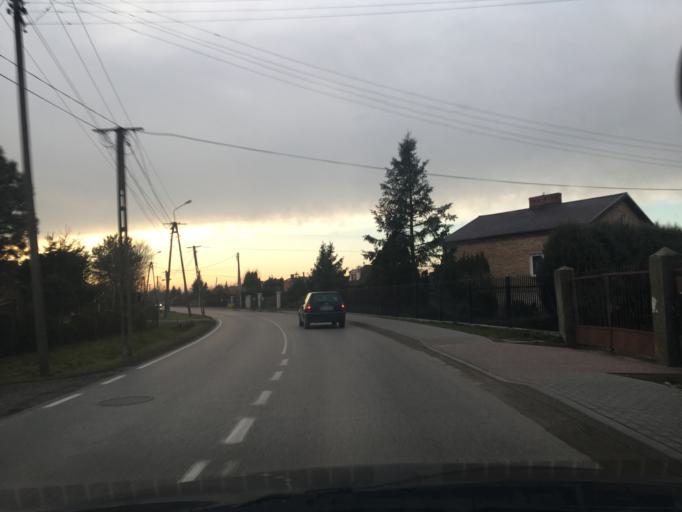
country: PL
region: Masovian Voivodeship
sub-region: Powiat piaseczynski
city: Lesznowola
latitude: 52.0419
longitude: 20.9684
